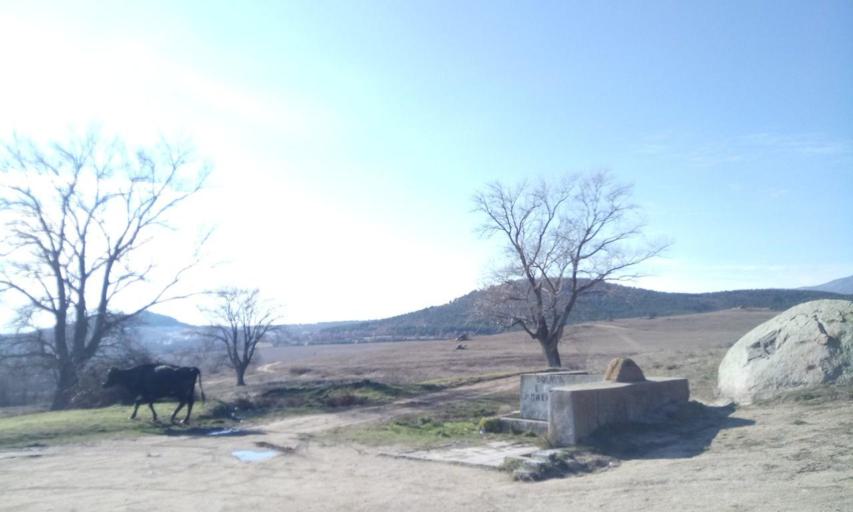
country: BG
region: Plovdiv
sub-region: Obshtina Khisarya
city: Khisarya
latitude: 42.5270
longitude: 24.7084
